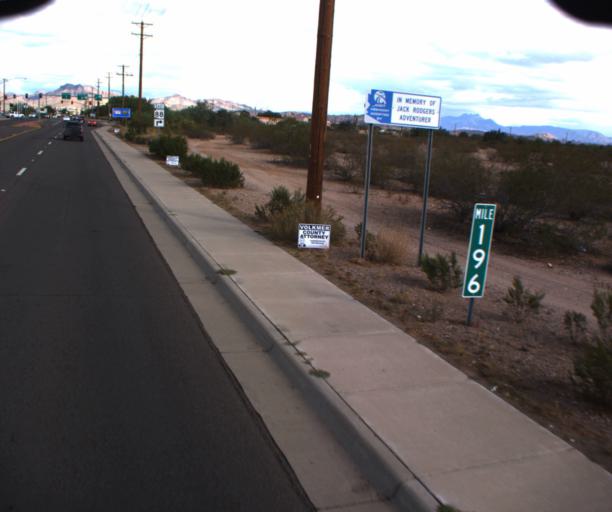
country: US
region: Arizona
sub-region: Pinal County
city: Apache Junction
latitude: 33.4171
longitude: -111.5460
